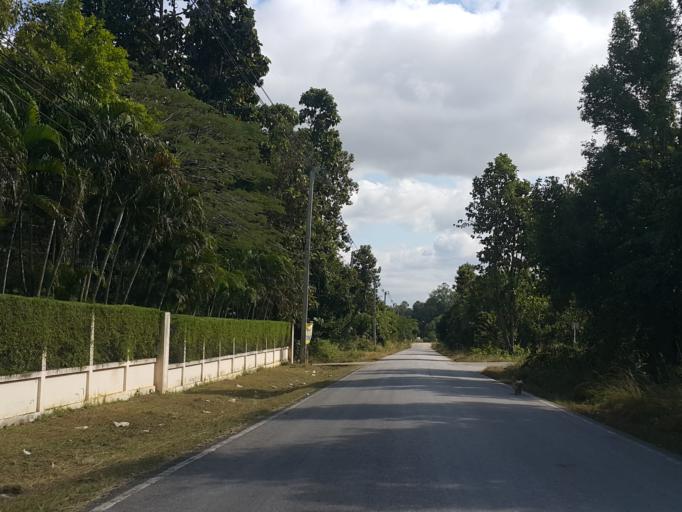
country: TH
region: Lampang
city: Hang Chat
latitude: 18.3307
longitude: 99.3873
